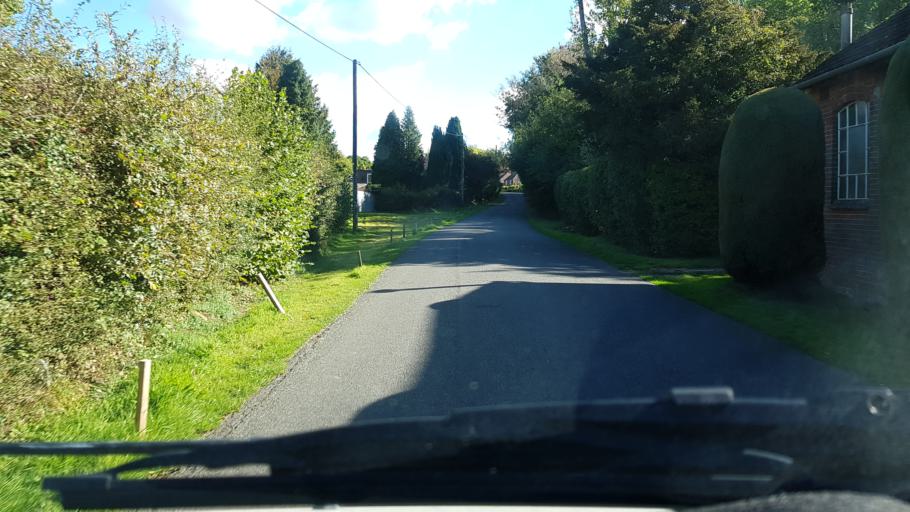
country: GB
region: England
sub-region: Surrey
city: Chiddingfold
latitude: 51.0872
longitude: -0.6055
